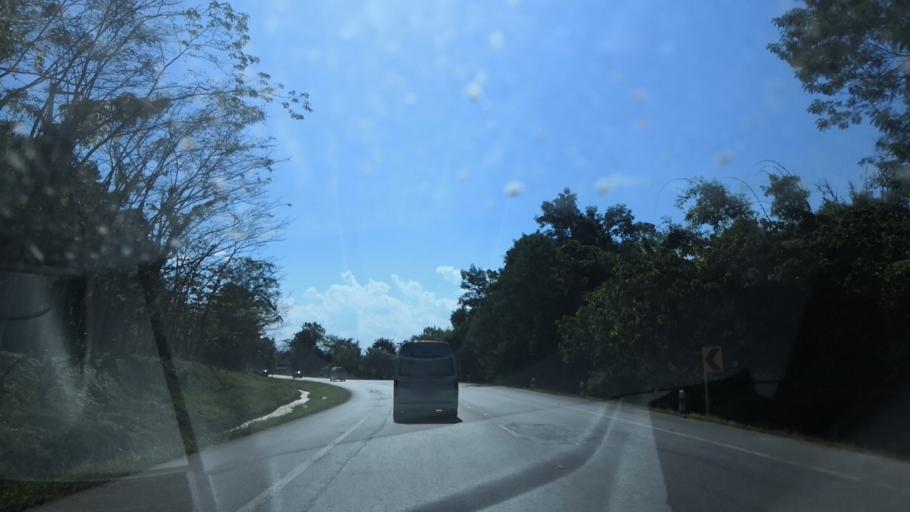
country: TH
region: Chiang Rai
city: Mae Suai
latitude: 19.5120
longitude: 99.4772
